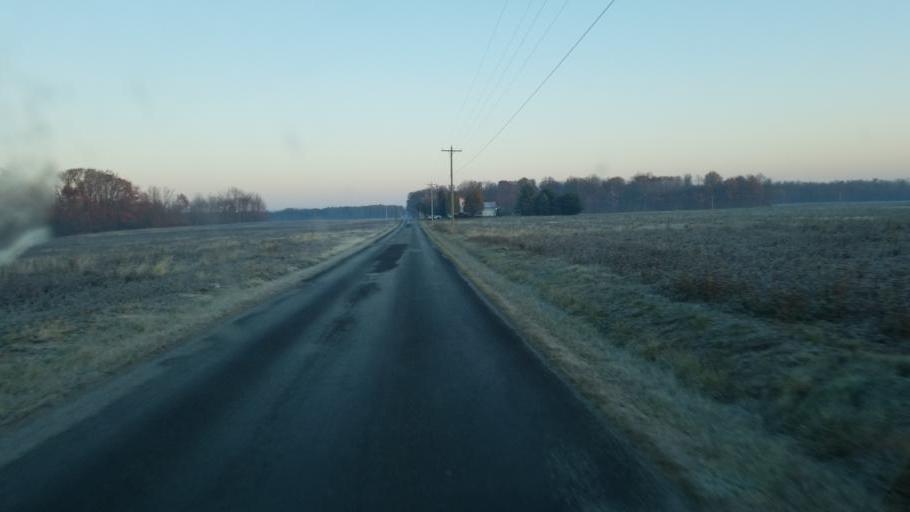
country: US
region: Ohio
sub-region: Wayne County
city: West Salem
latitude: 40.9697
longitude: -82.0779
